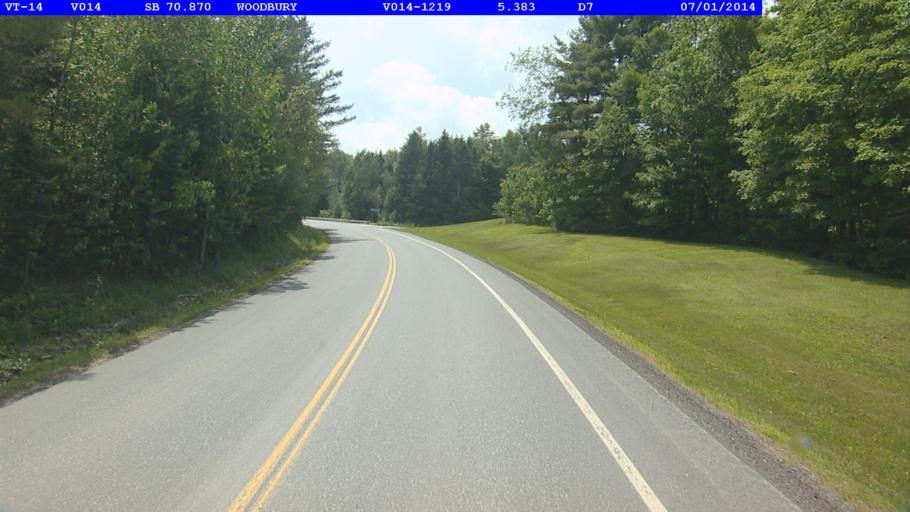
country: US
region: Vermont
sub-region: Caledonia County
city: Hardwick
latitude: 44.4641
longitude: -72.4151
